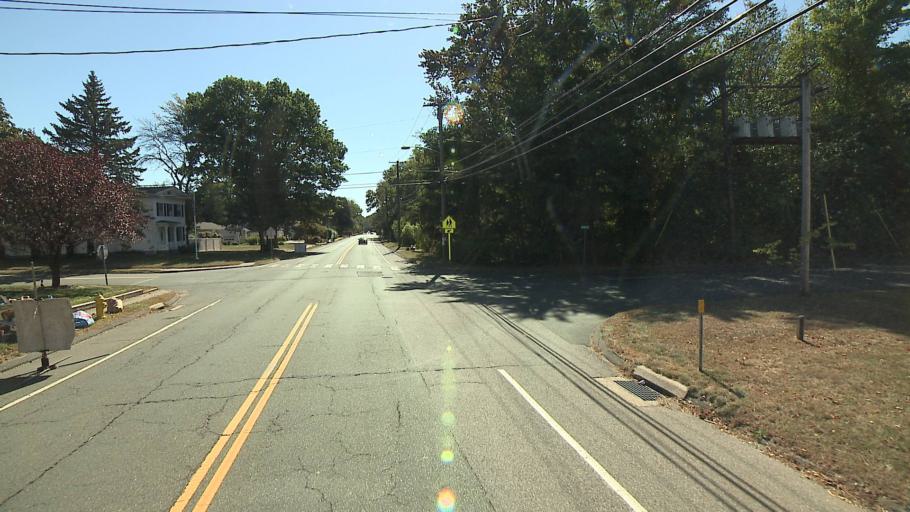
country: US
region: Connecticut
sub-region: New Haven County
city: City of Milford (balance)
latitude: 41.2364
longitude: -73.0569
